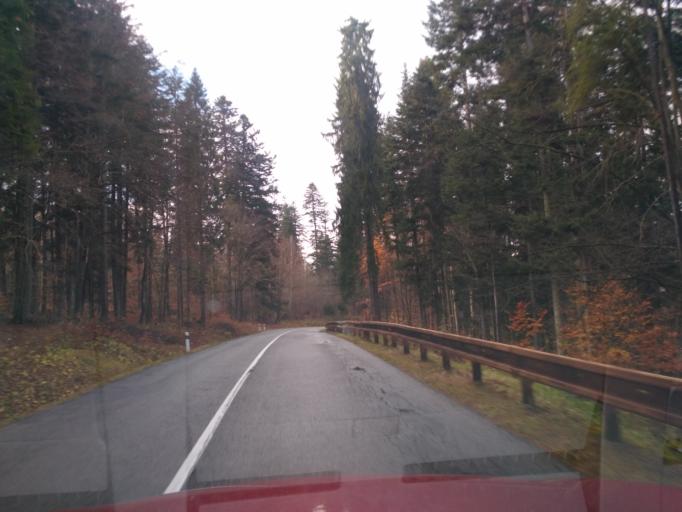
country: SK
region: Kosicky
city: Medzev
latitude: 48.7917
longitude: 20.7526
